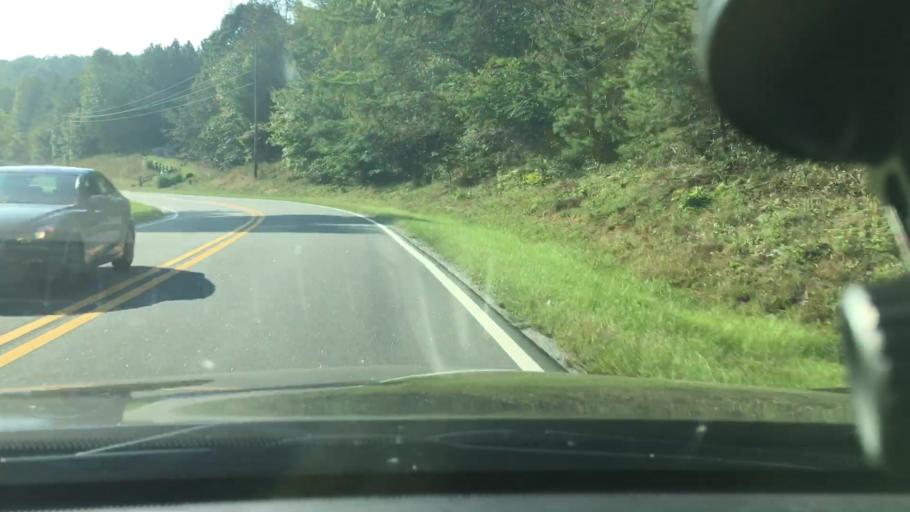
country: US
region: North Carolina
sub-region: Rutherford County
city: Rutherfordton
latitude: 35.3251
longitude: -82.0789
